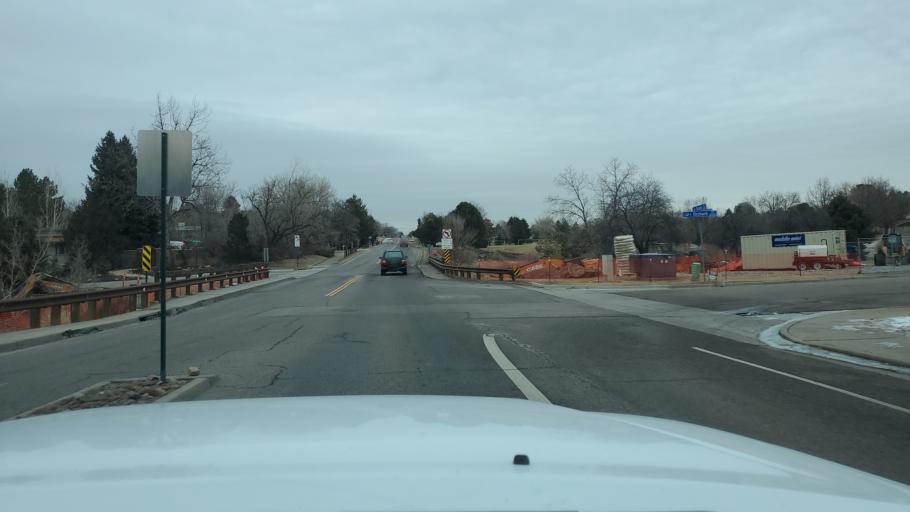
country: US
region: Colorado
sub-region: Arapahoe County
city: Castlewood
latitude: 39.6095
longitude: -104.9170
